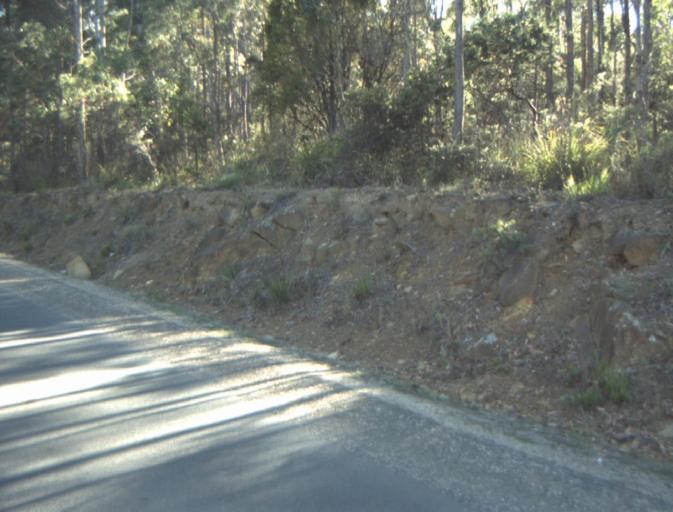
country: AU
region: Tasmania
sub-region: Launceston
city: Mayfield
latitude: -41.3231
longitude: 147.1874
